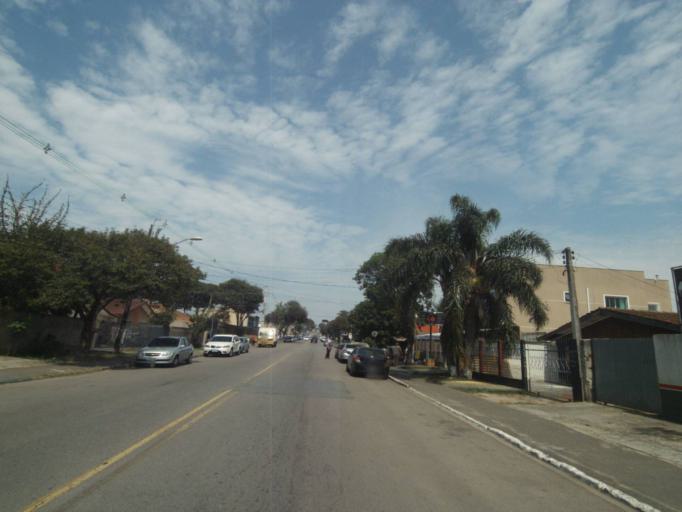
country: BR
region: Parana
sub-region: Pinhais
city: Pinhais
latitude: -25.4225
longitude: -49.1995
